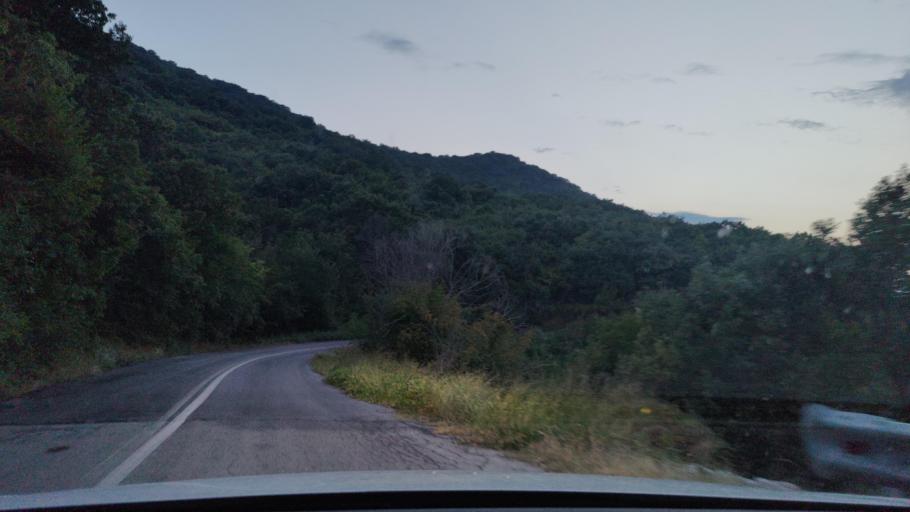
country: GR
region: Central Macedonia
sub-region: Nomos Serron
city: Chrysochorafa
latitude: 41.1769
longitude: 23.1674
